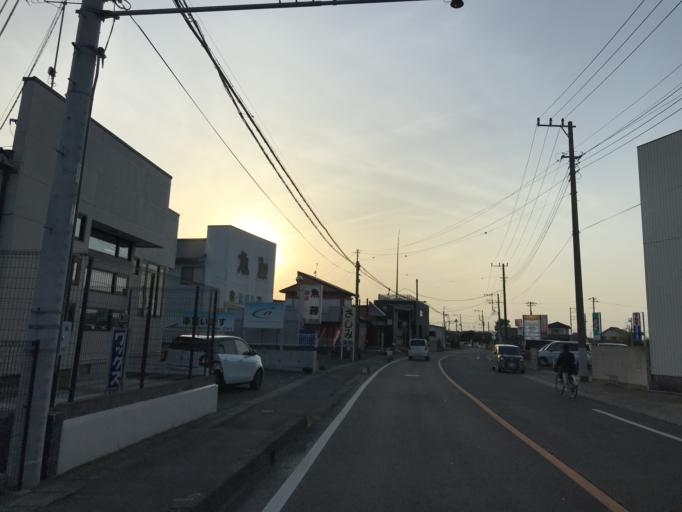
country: JP
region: Ibaraki
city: Katsuta
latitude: 36.3686
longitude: 140.5059
